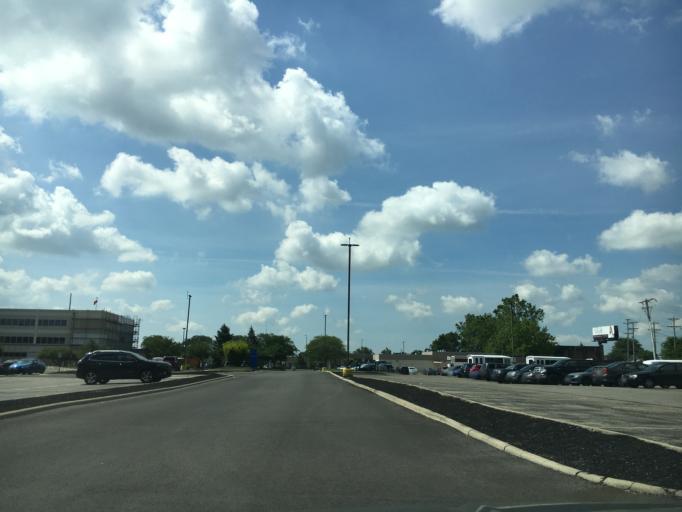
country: US
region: Ohio
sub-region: Franklin County
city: Lincoln Village
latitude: 39.9540
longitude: -83.1390
